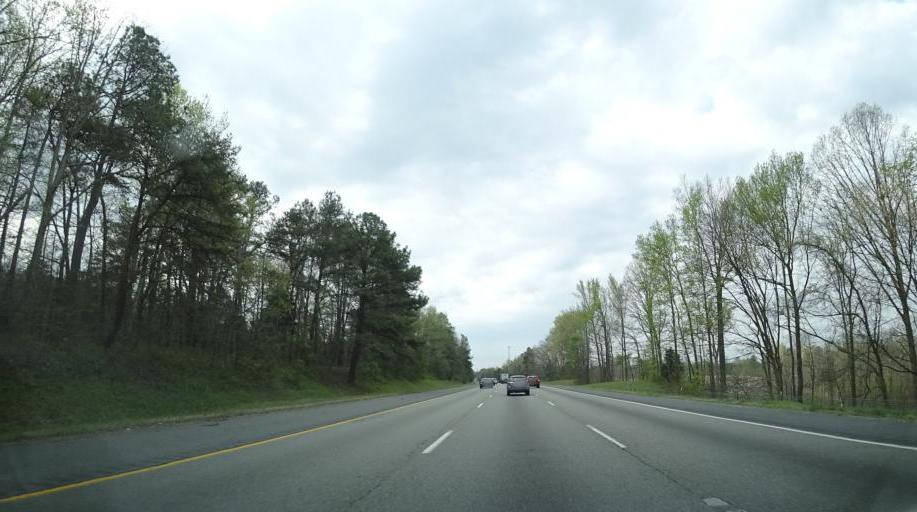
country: US
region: Virginia
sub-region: Hanover County
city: Ashland
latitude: 37.8954
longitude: -77.4596
